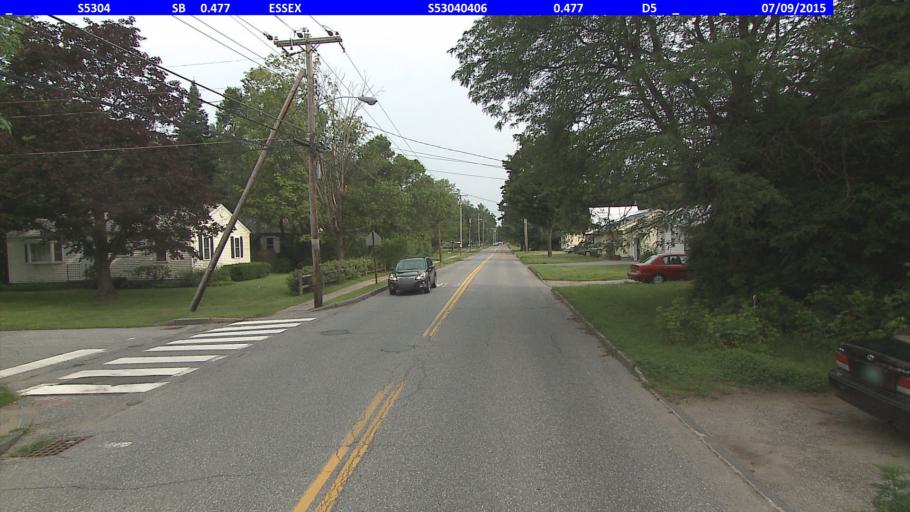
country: US
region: Vermont
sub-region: Chittenden County
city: Essex Junction
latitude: 44.4932
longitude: -73.1271
